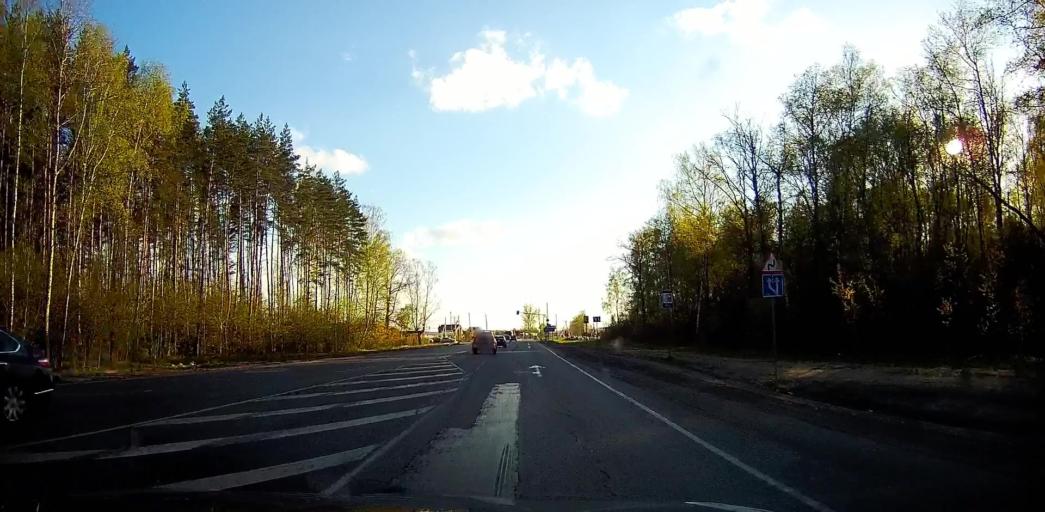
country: RU
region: Moskovskaya
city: Bronnitsy
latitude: 55.3930
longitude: 38.2052
